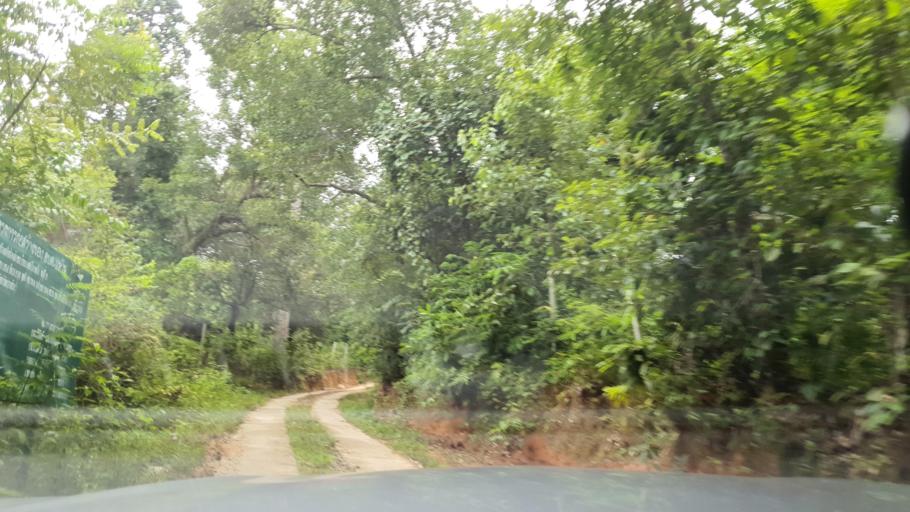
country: TH
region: Chiang Mai
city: Mae Wang
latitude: 18.6640
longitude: 98.6212
